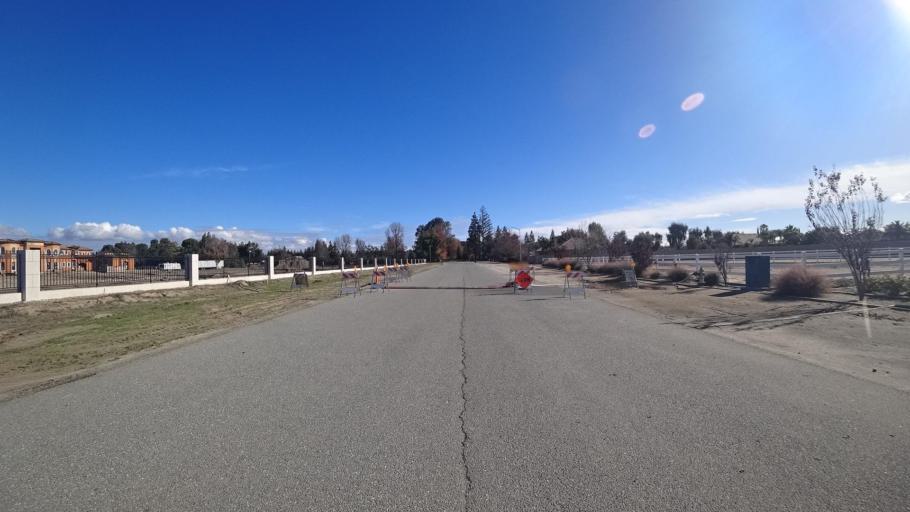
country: US
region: California
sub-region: Kern County
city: Rosedale
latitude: 35.3598
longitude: -119.1919
